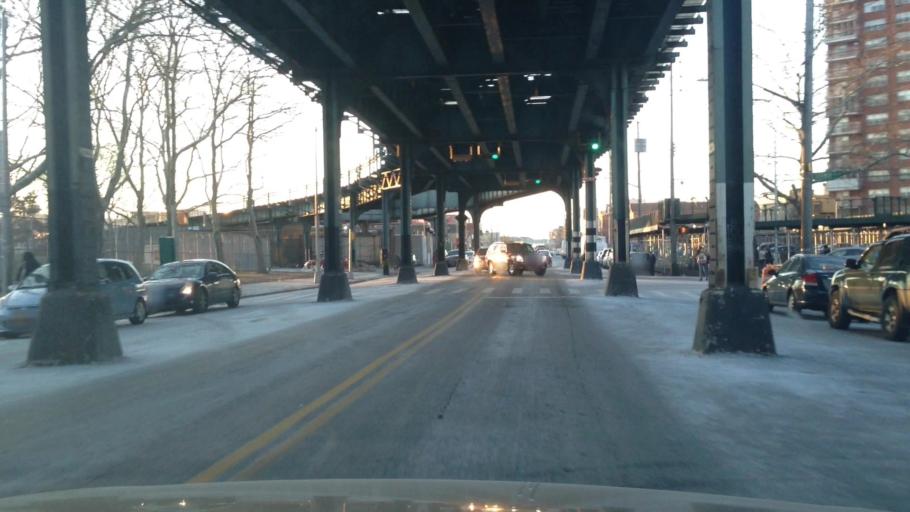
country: US
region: New York
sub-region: Kings County
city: Coney Island
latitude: 40.5880
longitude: -73.9836
